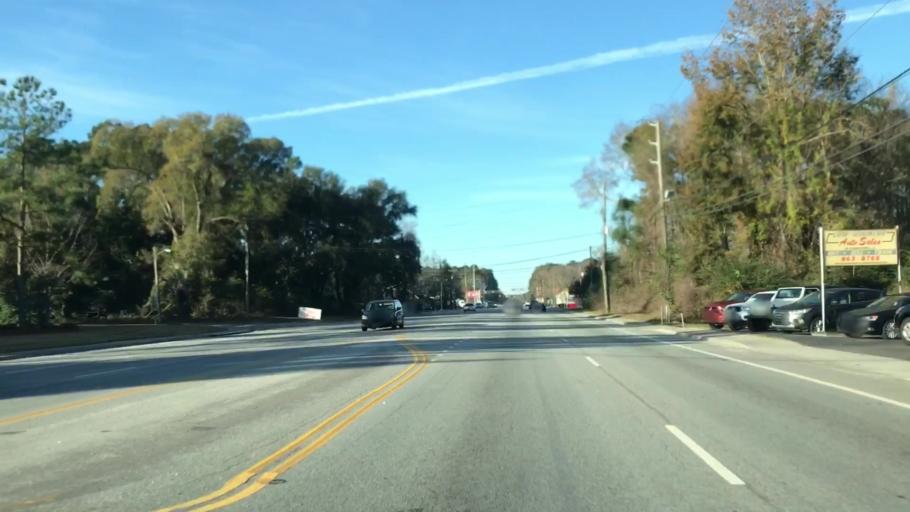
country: US
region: South Carolina
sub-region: Berkeley County
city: Ladson
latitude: 32.9864
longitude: -80.1063
